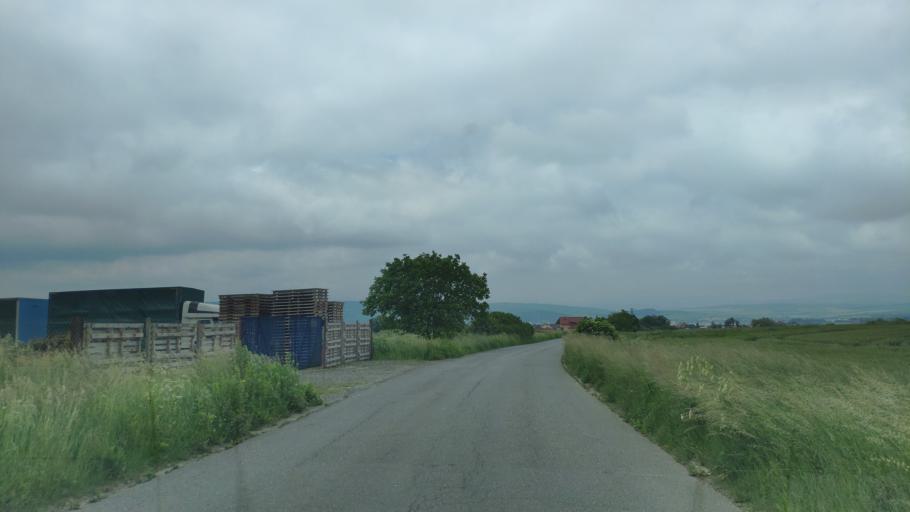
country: SK
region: Presovsky
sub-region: Okres Presov
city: Presov
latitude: 48.9969
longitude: 21.2980
